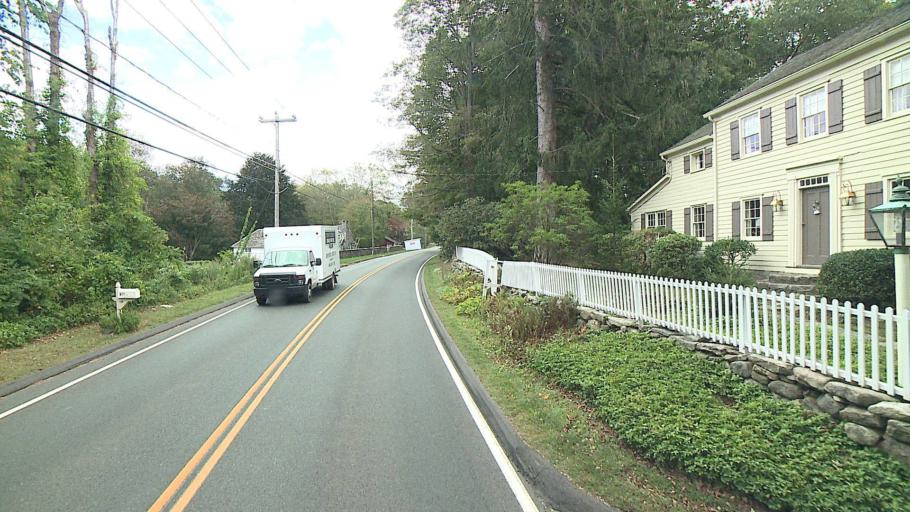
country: US
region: Connecticut
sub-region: Fairfield County
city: Georgetown
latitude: 41.2316
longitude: -73.4808
